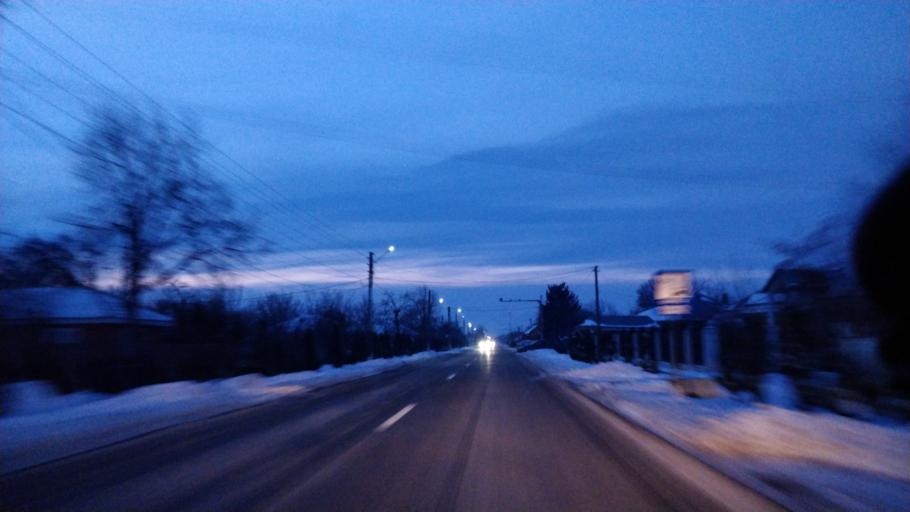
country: RO
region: Vrancea
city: Vulturu de Sus
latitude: 45.6143
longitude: 27.4333
